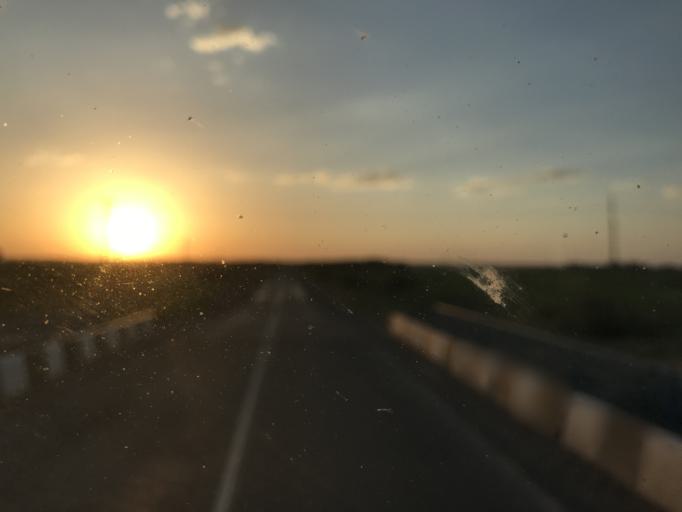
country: UZ
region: Toshkent
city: Yangiyul
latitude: 41.3819
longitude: 68.7754
